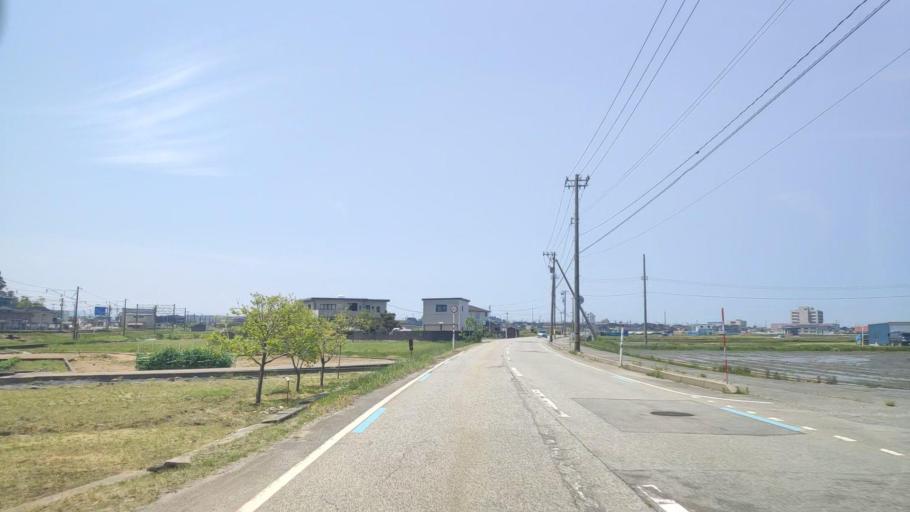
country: JP
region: Toyama
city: Nyuzen
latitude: 36.9618
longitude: 137.5724
